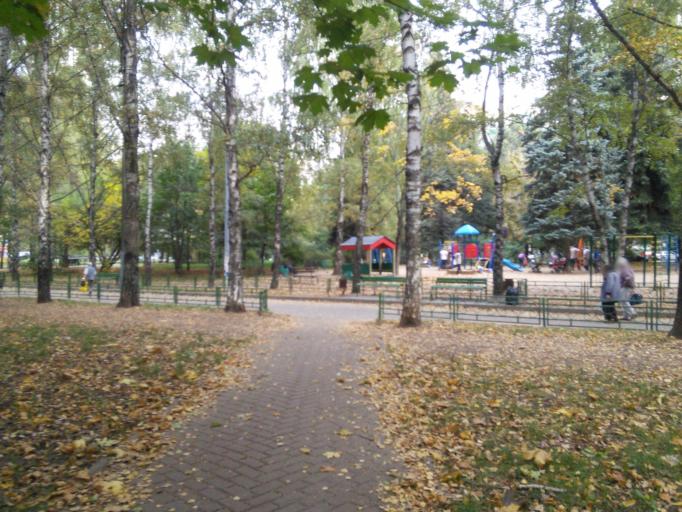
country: RU
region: Moskovskaya
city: Levoberezhnyy
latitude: 55.8604
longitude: 37.4742
